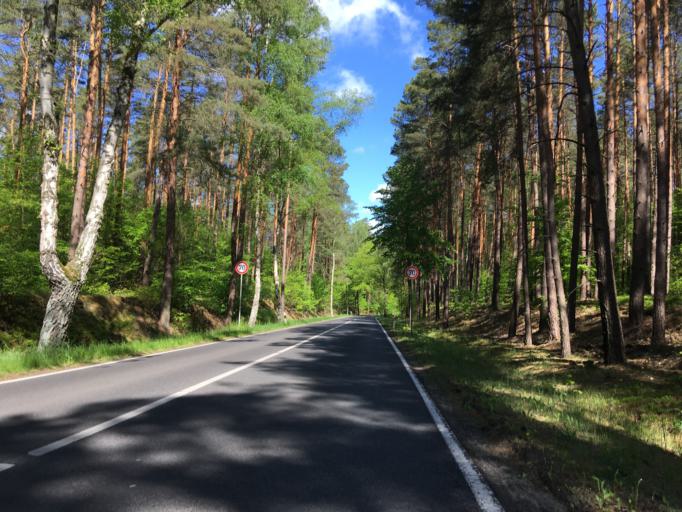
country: DE
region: Brandenburg
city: Birkenwerder
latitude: 52.7145
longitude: 13.3474
